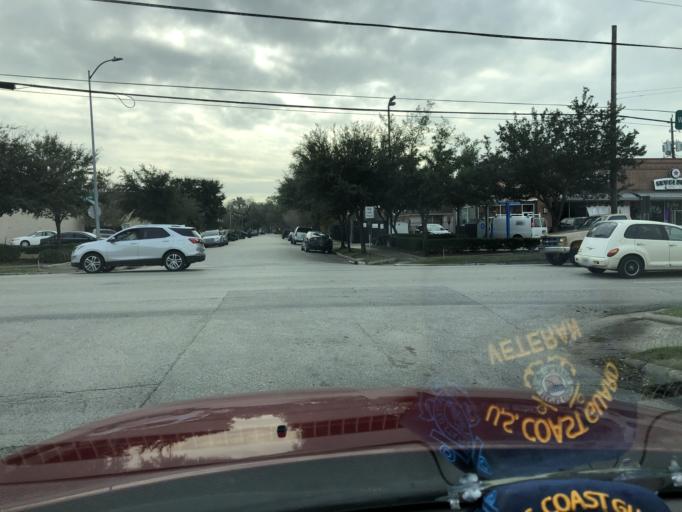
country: US
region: Texas
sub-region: Harris County
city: Houston
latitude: 29.7903
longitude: -95.4090
